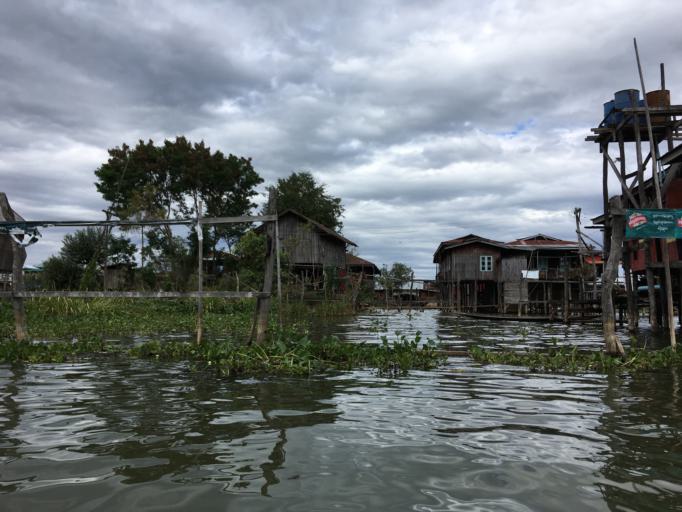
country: MM
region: Shan
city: Taunggyi
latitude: 20.4585
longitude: 96.9064
